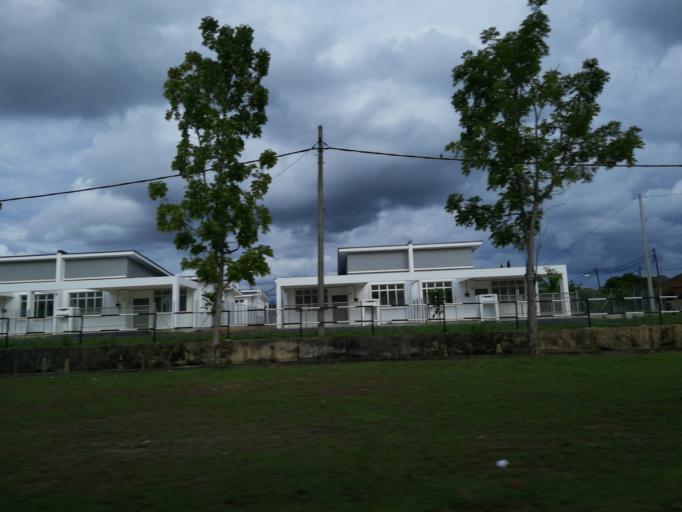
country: MY
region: Penang
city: Tasek Glugor
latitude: 5.4994
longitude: 100.6241
